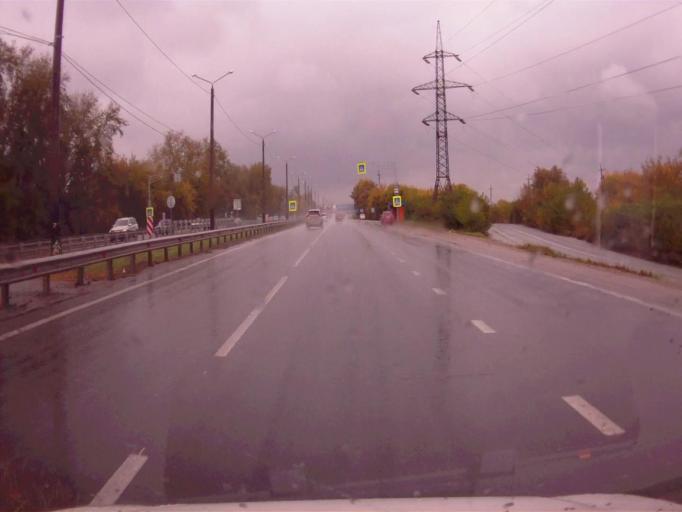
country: RU
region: Chelyabinsk
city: Dolgoderevenskoye
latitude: 55.2567
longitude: 61.3518
